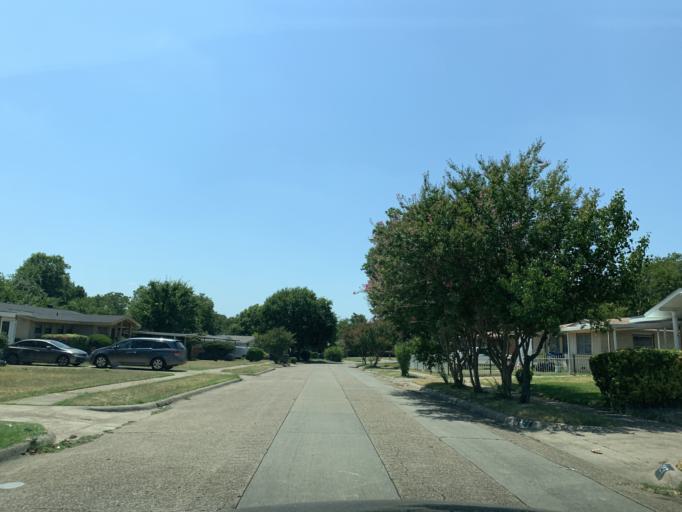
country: US
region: Texas
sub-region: Dallas County
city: Dallas
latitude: 32.6860
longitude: -96.8038
